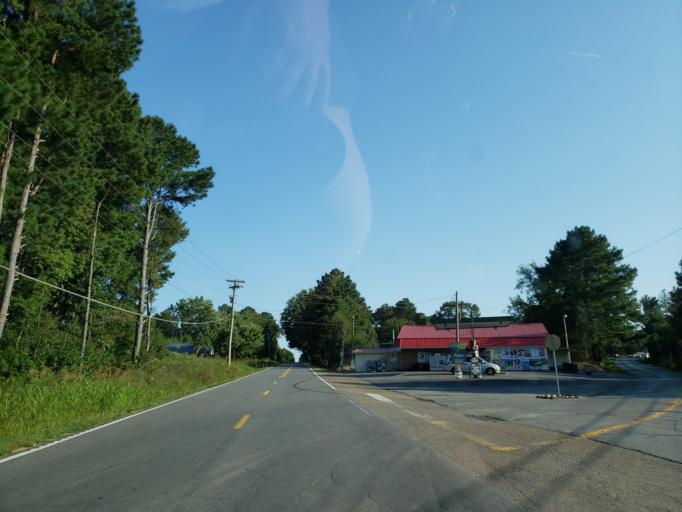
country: US
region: Tennessee
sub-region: Bradley County
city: Wildwood Lake
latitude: 35.0310
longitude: -84.7998
